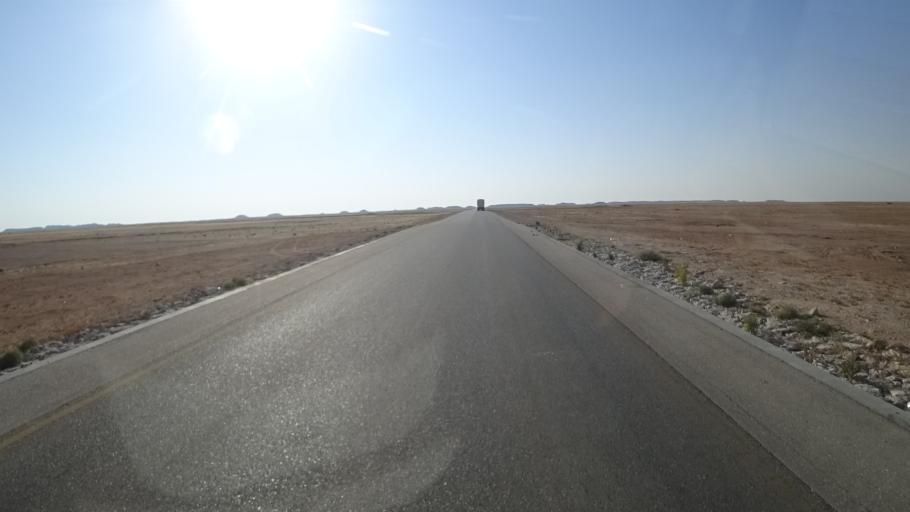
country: OM
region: Zufar
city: Salalah
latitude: 17.6427
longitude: 53.8443
